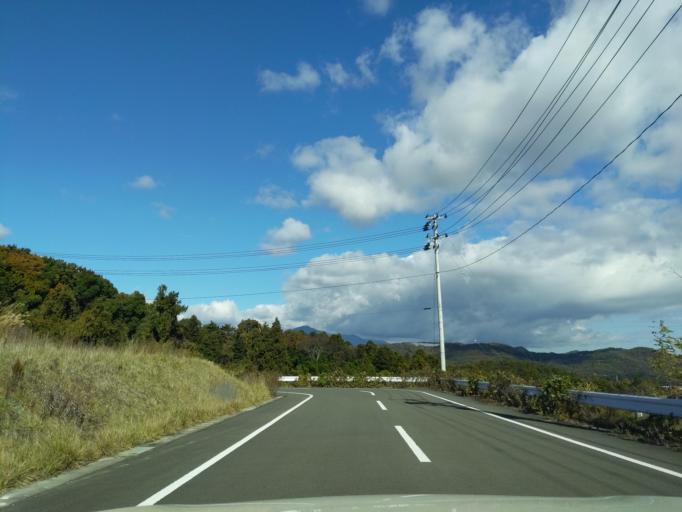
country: JP
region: Fukushima
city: Koriyama
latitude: 37.4645
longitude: 140.3035
